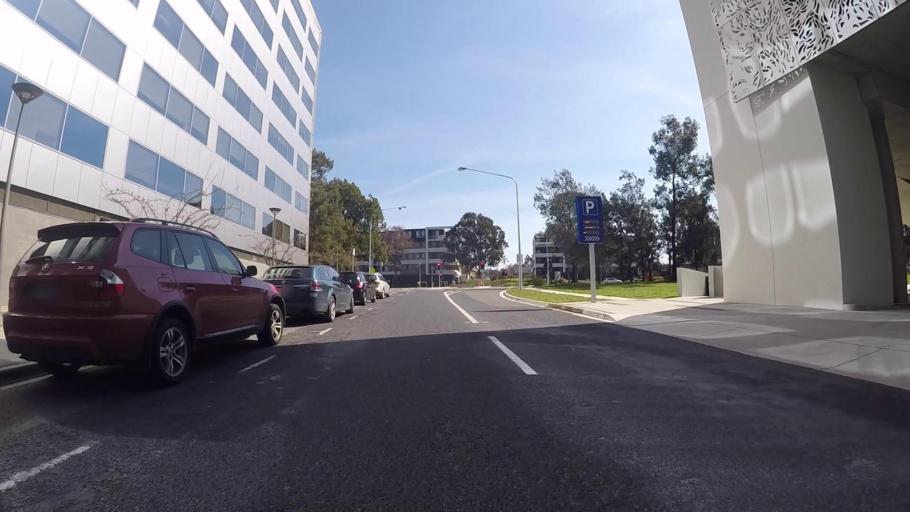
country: AU
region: Australian Capital Territory
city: Forrest
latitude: -35.3423
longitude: 149.0834
